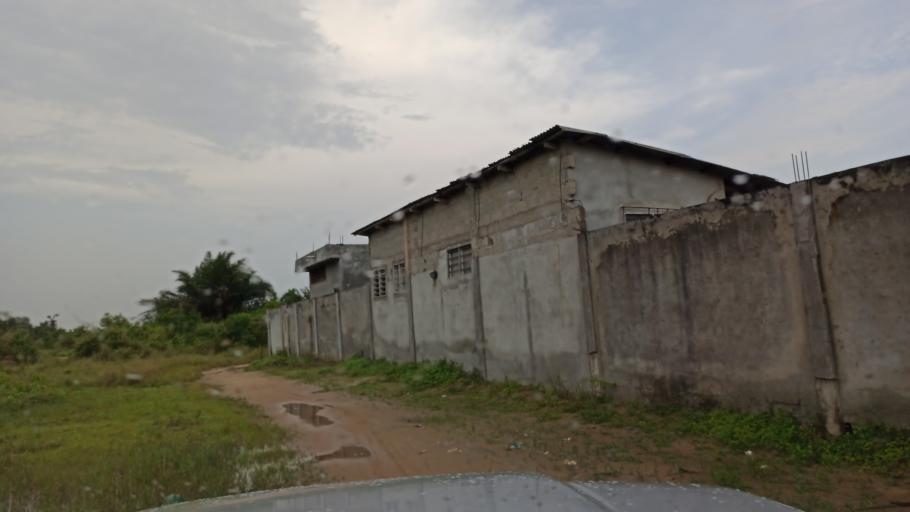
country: BJ
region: Queme
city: Porto-Novo
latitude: 6.4536
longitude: 2.6696
